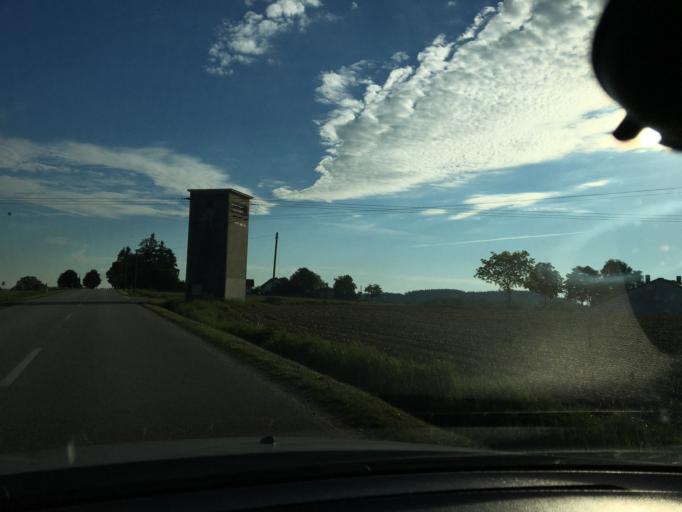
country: DE
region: Bavaria
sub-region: Lower Bavaria
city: Stallwang
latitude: 48.5172
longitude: 12.2237
